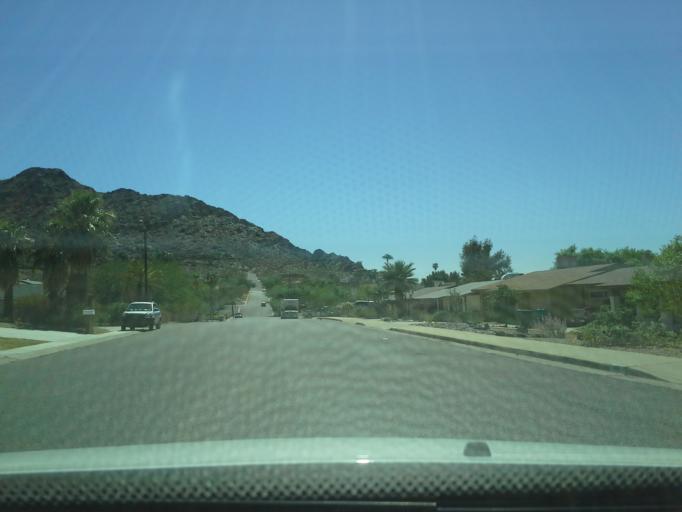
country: US
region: Arizona
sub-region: Maricopa County
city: Paradise Valley
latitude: 33.5735
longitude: -112.0480
